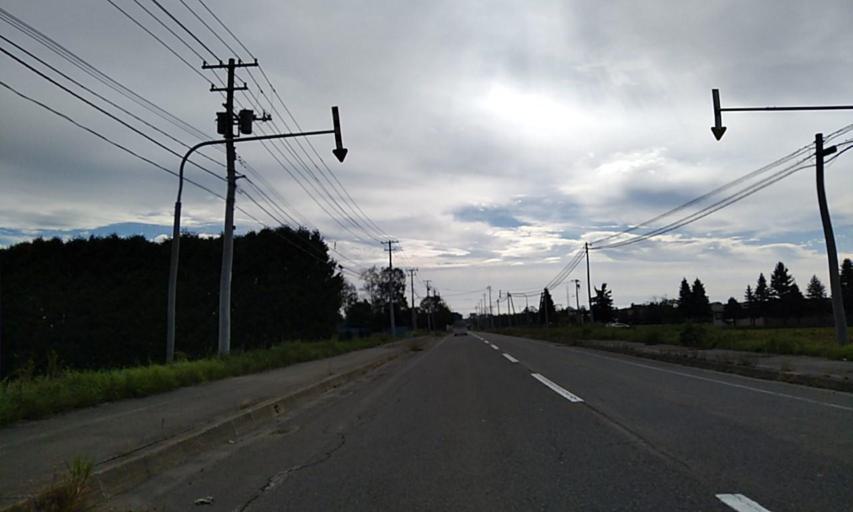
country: JP
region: Hokkaido
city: Obihiro
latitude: 42.8451
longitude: 143.1755
